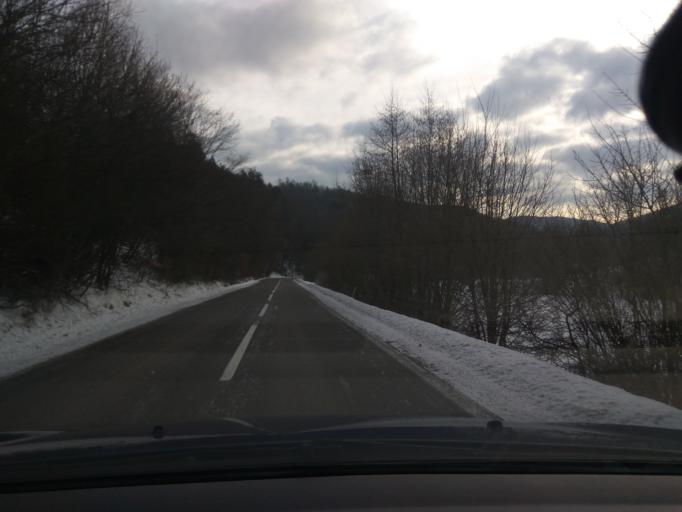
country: SK
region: Banskobystricky
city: Nova Bana
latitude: 48.5132
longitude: 18.6114
